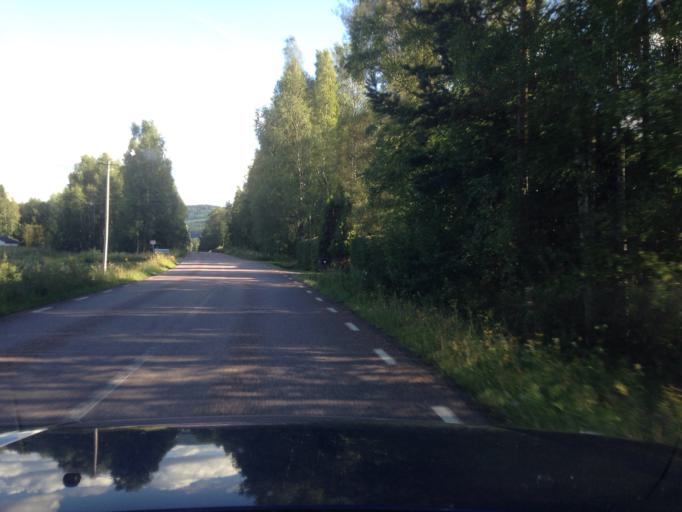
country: SE
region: Dalarna
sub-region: Ludvika Kommun
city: Grangesberg
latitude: 60.1620
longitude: 14.9718
